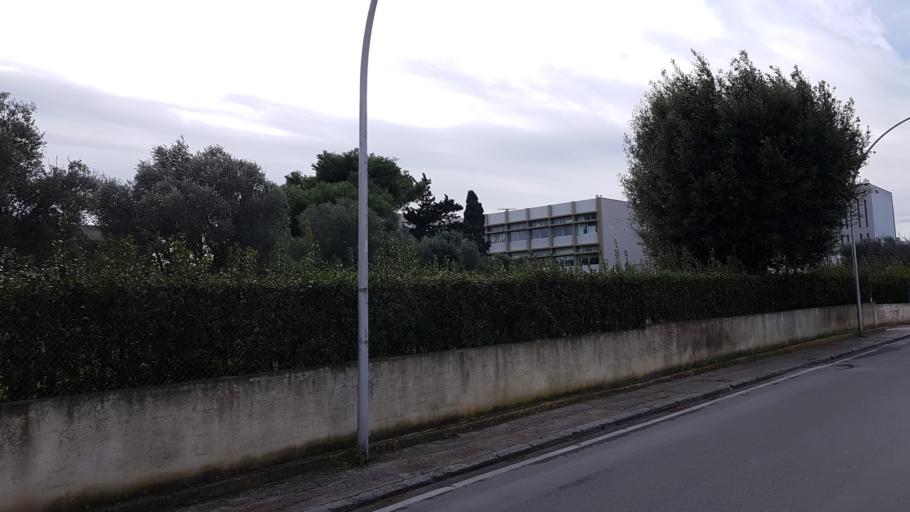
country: IT
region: Apulia
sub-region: Provincia di Brindisi
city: Brindisi
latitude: 40.6446
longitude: 17.9302
